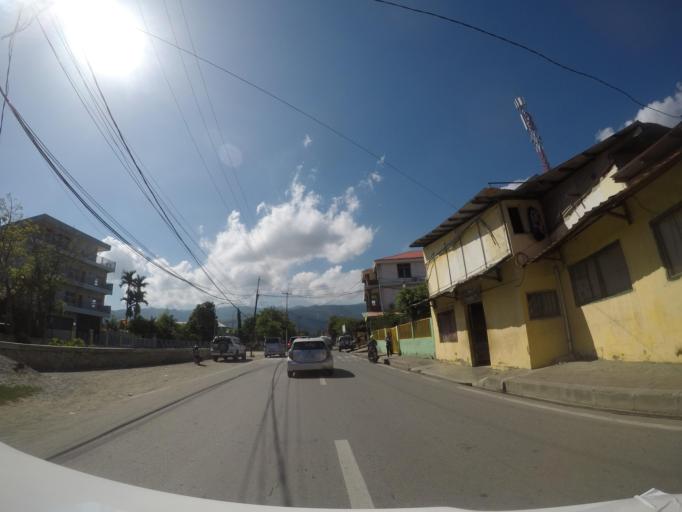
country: TL
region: Dili
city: Dili
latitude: -8.5494
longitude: 125.5896
